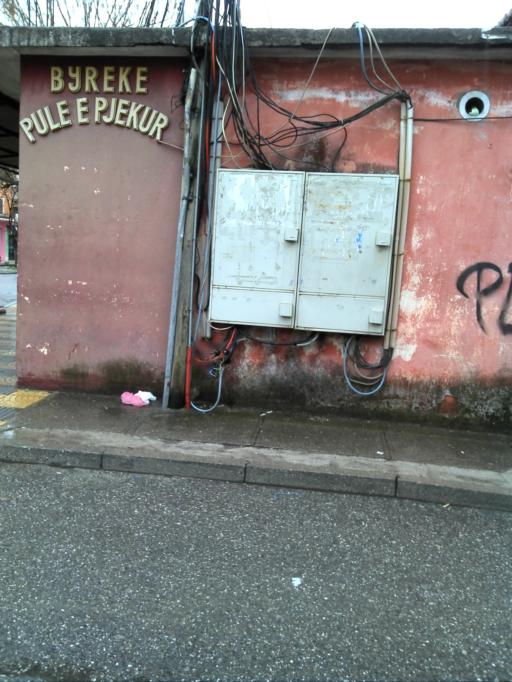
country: AL
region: Shkoder
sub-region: Rrethi i Shkodres
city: Shkoder
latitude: 42.0689
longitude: 19.5107
